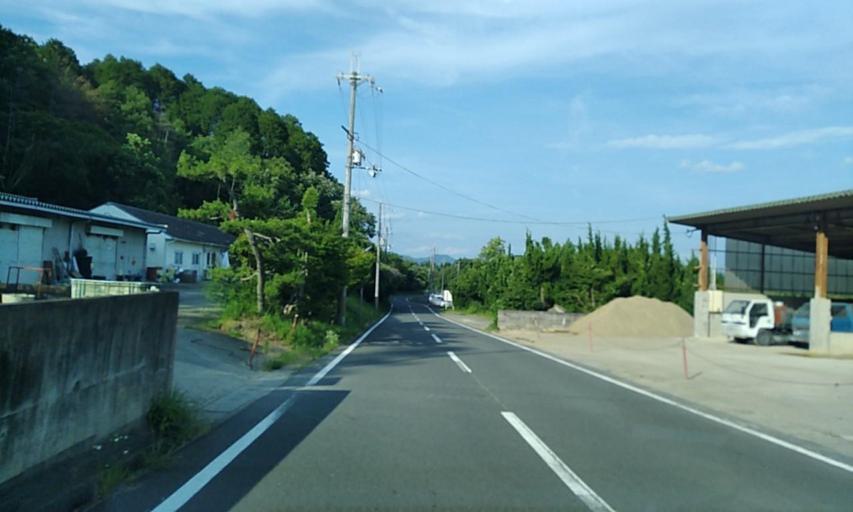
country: JP
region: Kyoto
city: Ayabe
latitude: 35.1633
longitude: 135.3772
